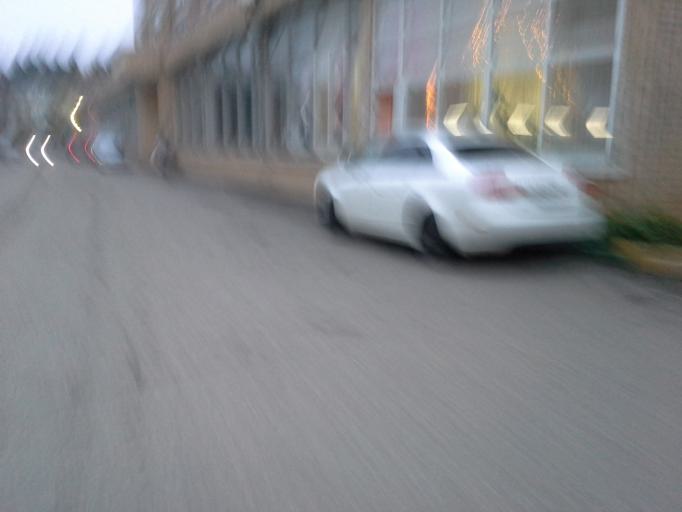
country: RU
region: Moskovskaya
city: Nazar'yevo
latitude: 55.7042
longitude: 37.0253
